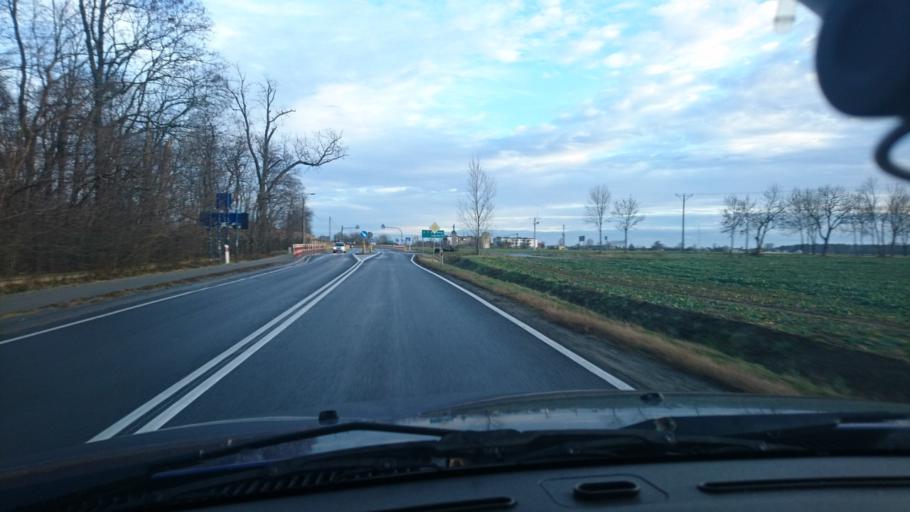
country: PL
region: Greater Poland Voivodeship
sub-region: Powiat kepinski
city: Slupia pod Kepnem
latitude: 51.2402
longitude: 18.0356
